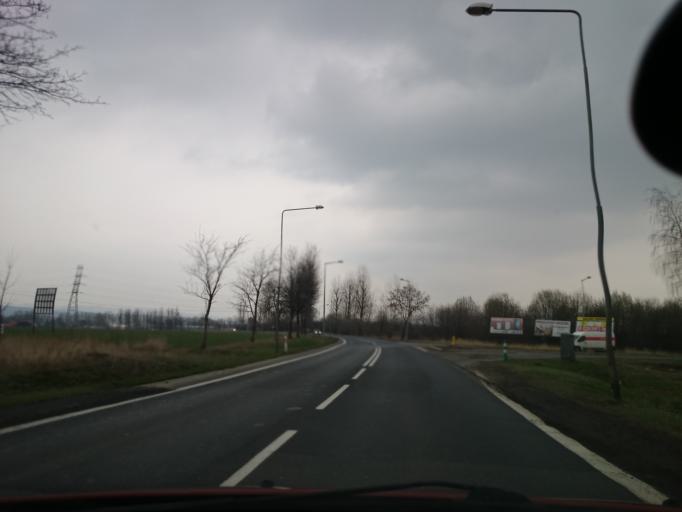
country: PL
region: Lower Silesian Voivodeship
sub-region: Powiat klodzki
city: Klodzko
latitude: 50.4389
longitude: 16.6244
